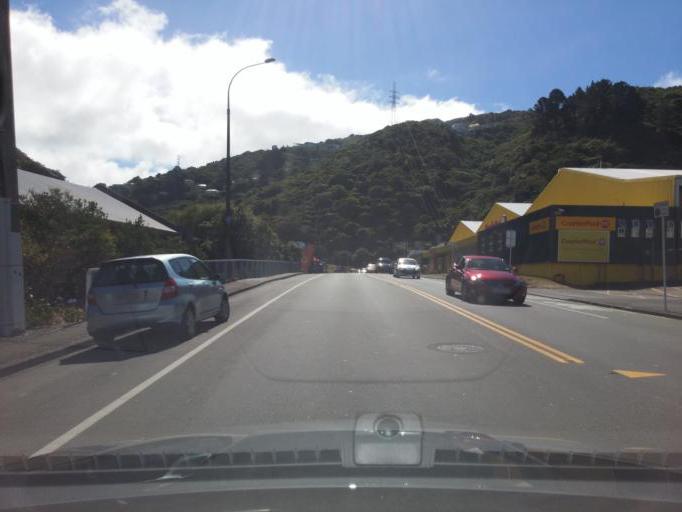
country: NZ
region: Wellington
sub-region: Wellington City
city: Wellington
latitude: -41.2591
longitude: 174.7882
